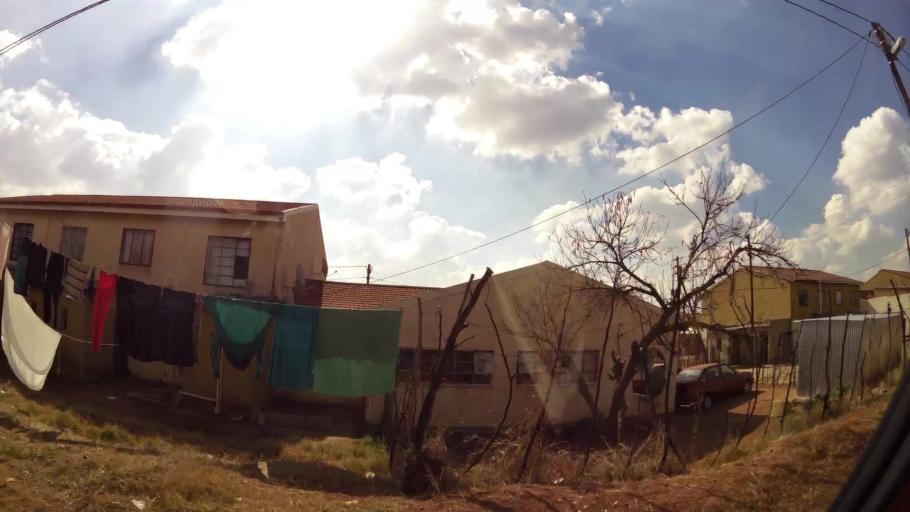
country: ZA
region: Gauteng
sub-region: City of Johannesburg Metropolitan Municipality
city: Roodepoort
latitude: -26.1848
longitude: 27.8410
